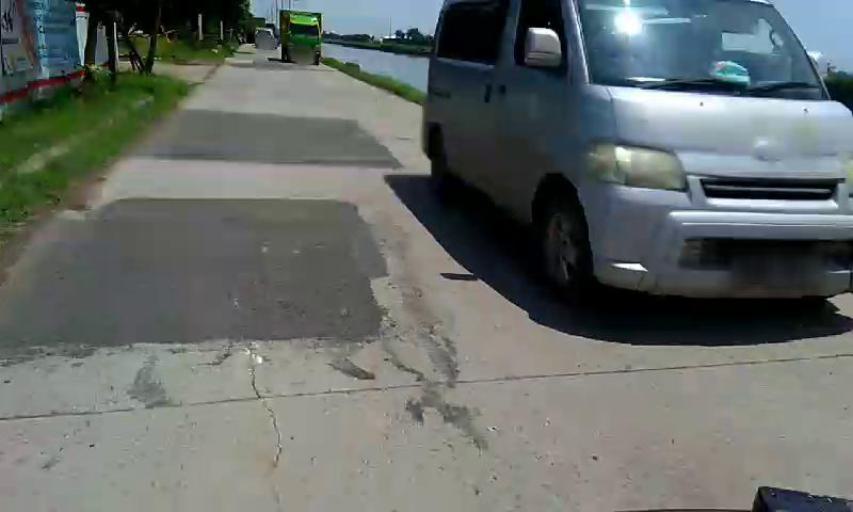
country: ID
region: West Java
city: Bekasi
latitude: -6.1189
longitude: 106.9691
